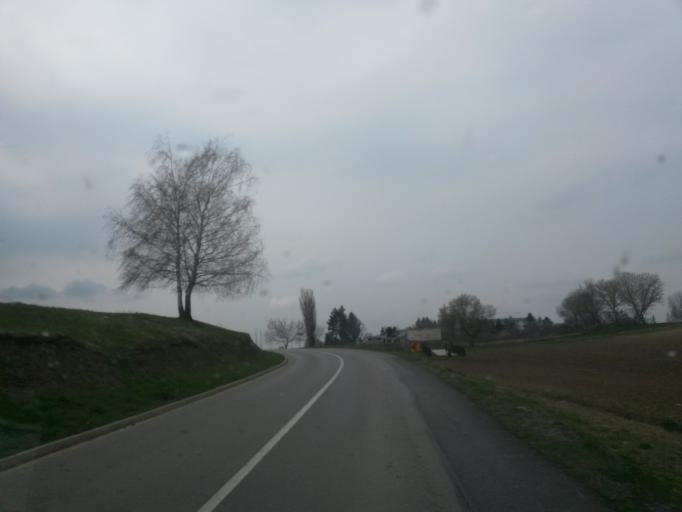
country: HR
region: Vukovarsko-Srijemska
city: Lovas
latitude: 45.2189
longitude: 19.1609
